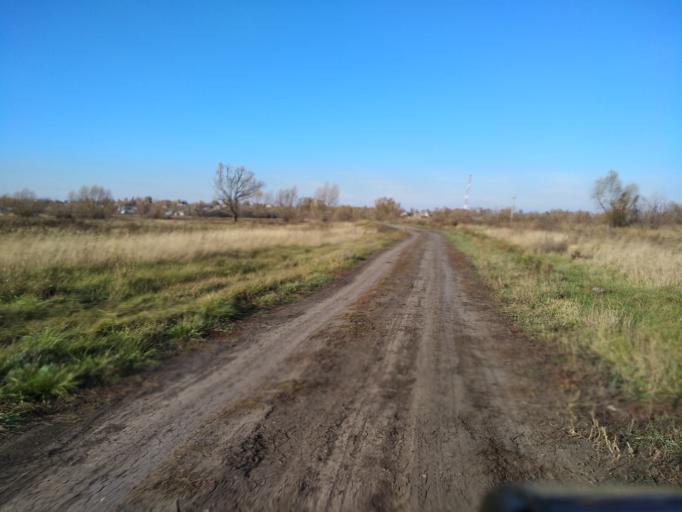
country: RU
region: Lipetsk
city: Dobrinka
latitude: 52.0271
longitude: 40.5553
